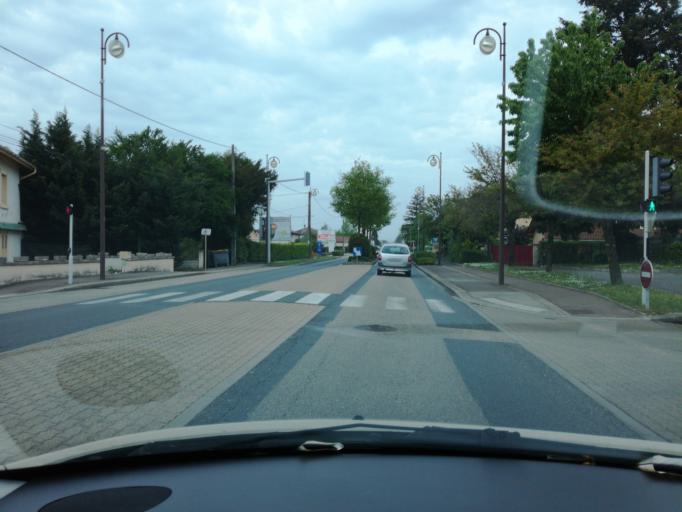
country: FR
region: Rhone-Alpes
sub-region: Departement de l'Ain
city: Peronnas
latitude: 46.1797
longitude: 5.2034
